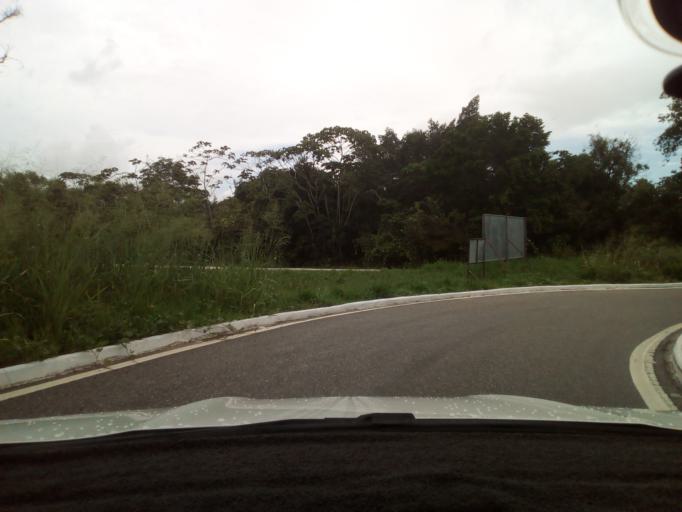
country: BR
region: Paraiba
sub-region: Cruz Do Espirito Santo
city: Cruz do Espirito Santo
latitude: -7.2001
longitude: -35.0765
